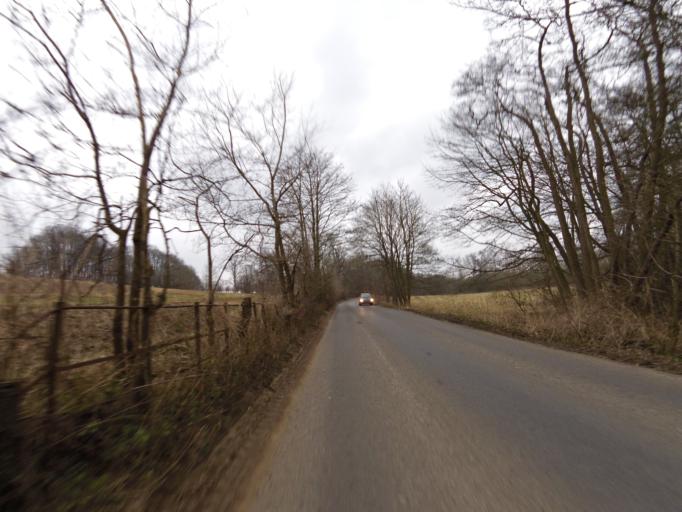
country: GB
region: England
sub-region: Suffolk
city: Wickham Market
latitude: 52.1678
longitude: 1.3550
